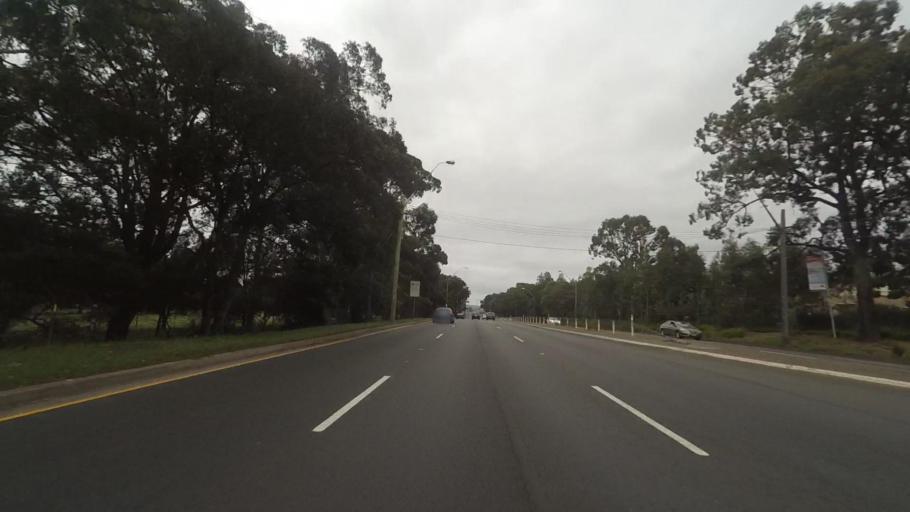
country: AU
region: New South Wales
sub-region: Auburn
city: Berala
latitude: -33.8779
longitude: 151.0411
